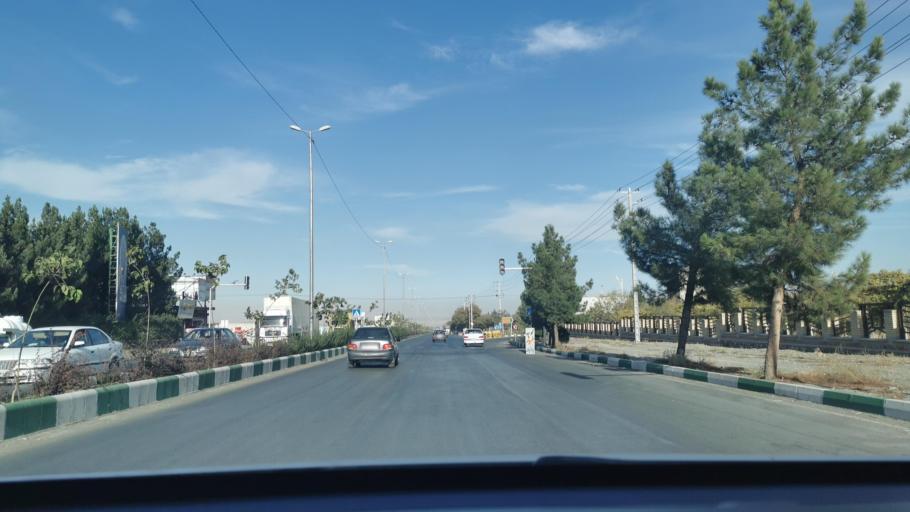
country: IR
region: Razavi Khorasan
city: Torqabeh
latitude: 36.4318
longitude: 59.4249
